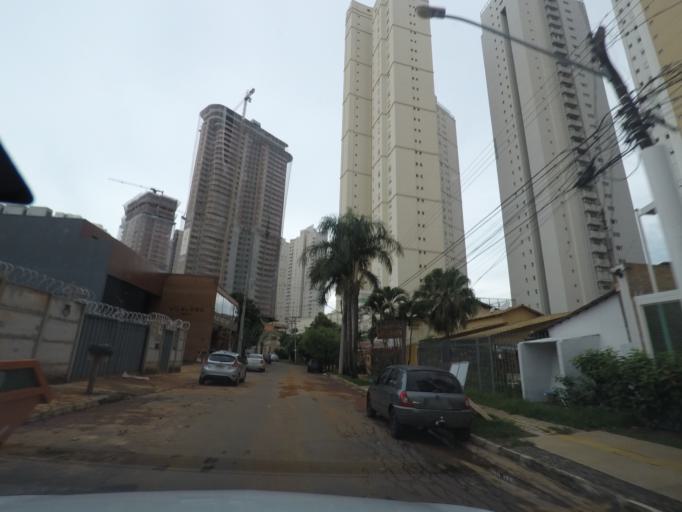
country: BR
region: Goias
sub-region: Goiania
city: Goiania
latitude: -16.7030
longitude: -49.2559
